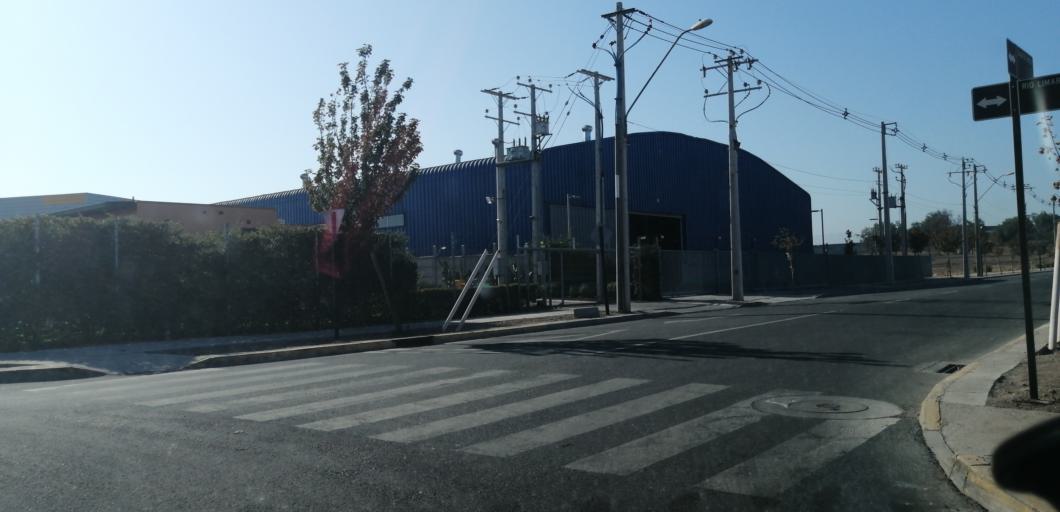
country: CL
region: Santiago Metropolitan
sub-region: Provincia de Santiago
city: Lo Prado
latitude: -33.4378
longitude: -70.7824
